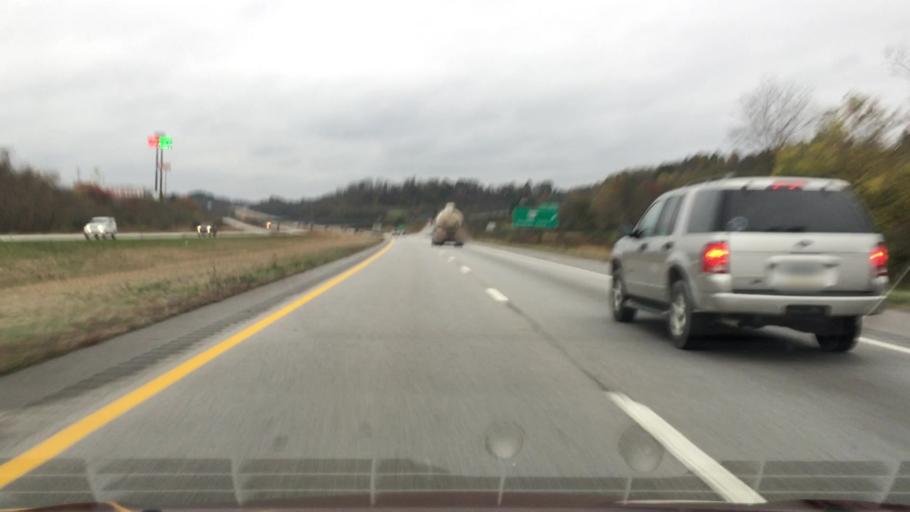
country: US
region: Ohio
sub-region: Belmont County
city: Barnesville
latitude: 40.0504
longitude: -81.3324
